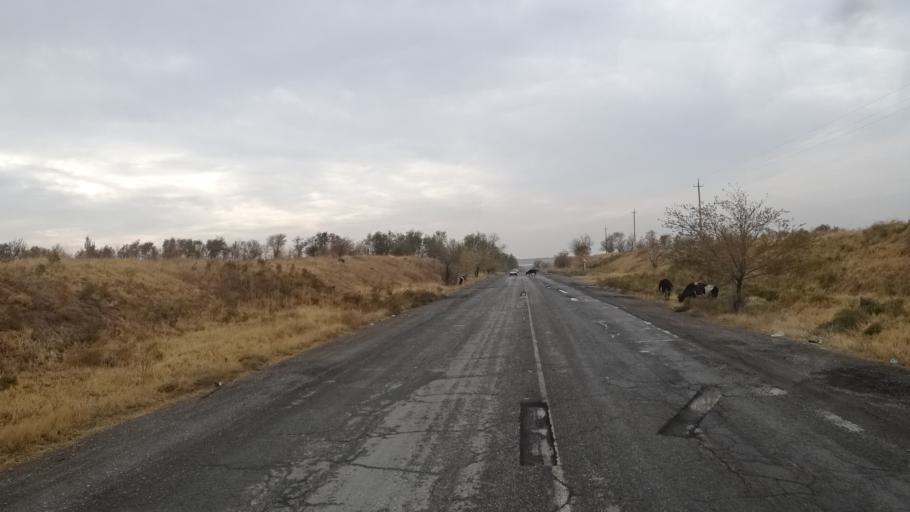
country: KZ
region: Ongtustik Qazaqstan
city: Aksu
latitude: 42.4316
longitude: 69.7122
